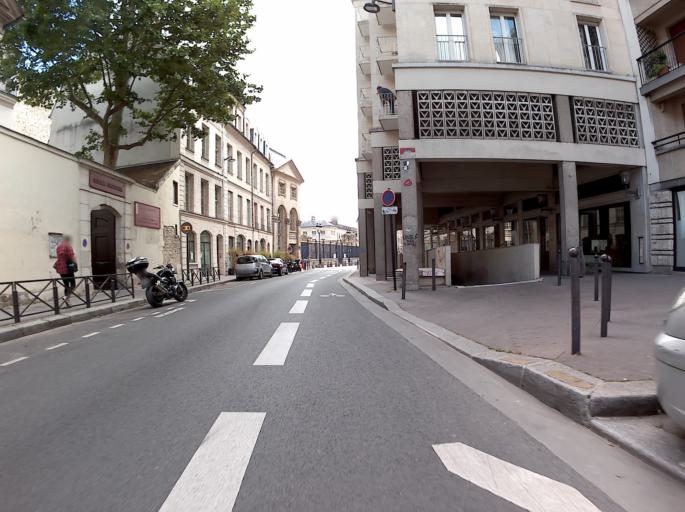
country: FR
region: Ile-de-France
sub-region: Paris
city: Paris
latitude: 48.8418
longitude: 2.3412
